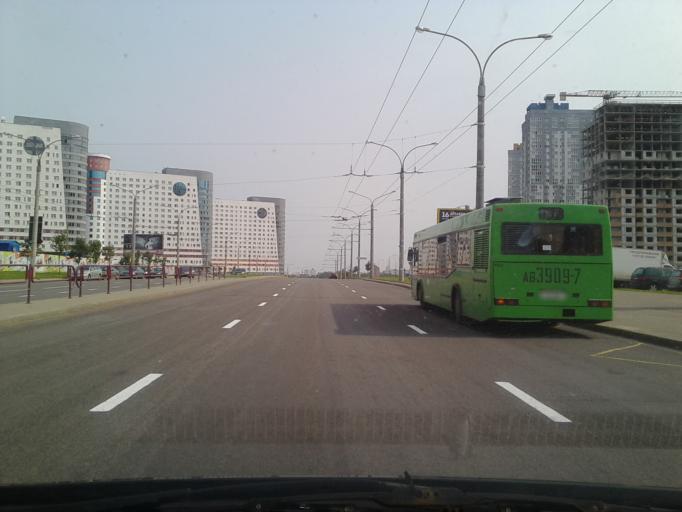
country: BY
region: Minsk
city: Novoye Medvezhino
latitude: 53.8562
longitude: 27.4788
